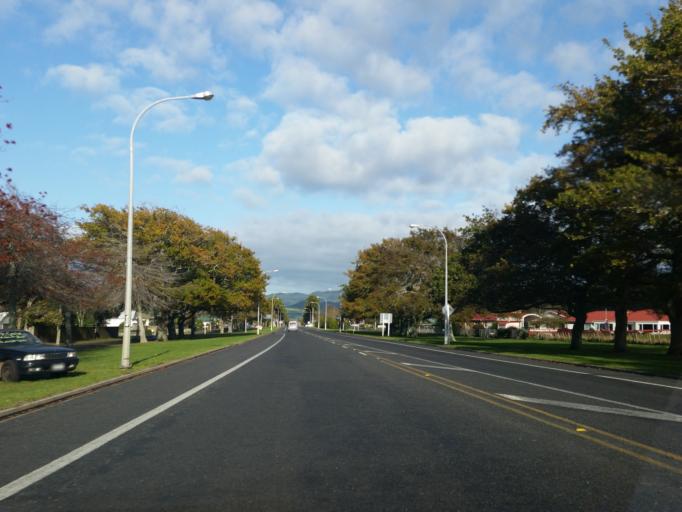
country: NZ
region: Waikato
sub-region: Hauraki District
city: Waihi
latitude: -37.3938
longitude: 175.8315
